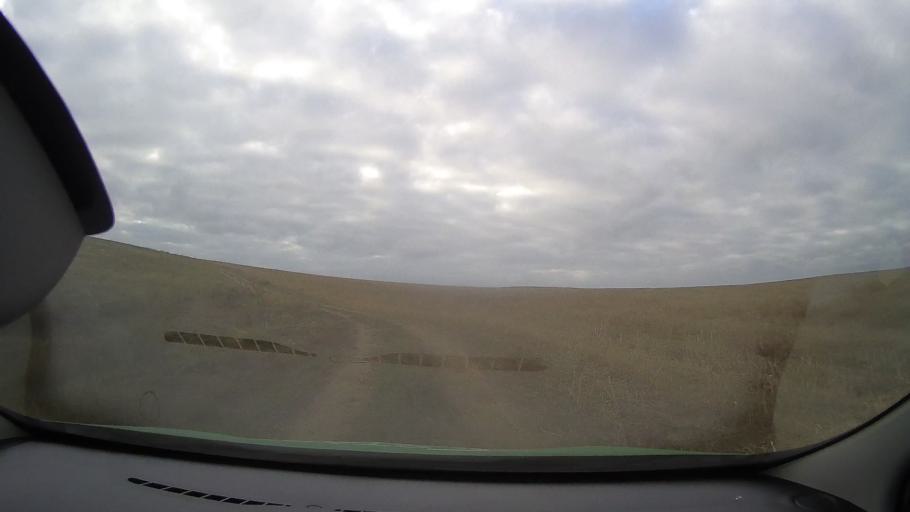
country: RO
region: Tulcea
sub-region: Comuna Jurilovca
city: Jurilovca
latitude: 44.7662
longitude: 28.9223
